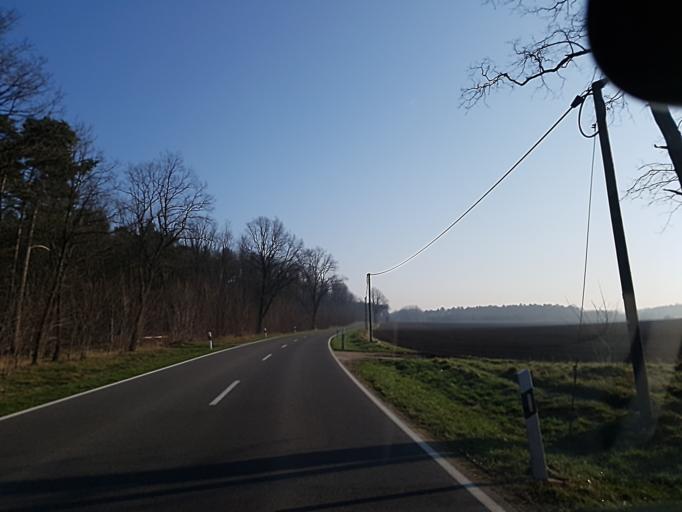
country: DE
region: Brandenburg
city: Bronkow
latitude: 51.6591
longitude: 13.9018
